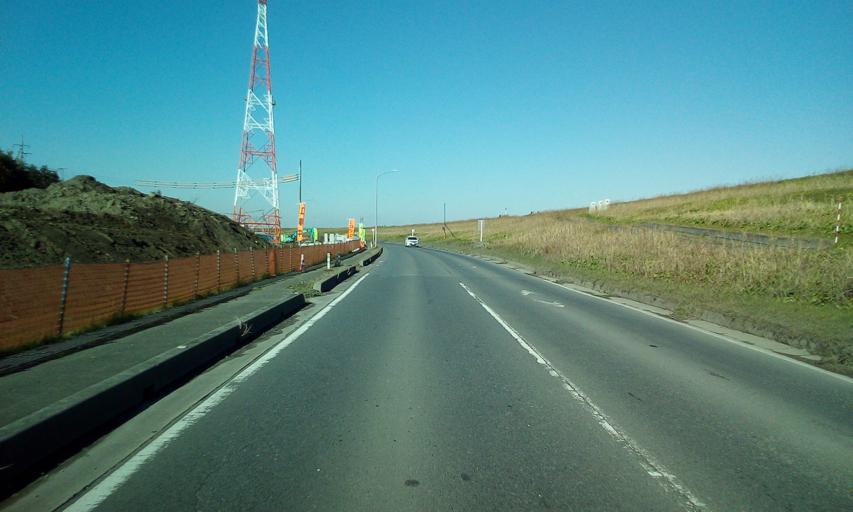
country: JP
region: Chiba
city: Noda
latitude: 35.9262
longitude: 139.8618
